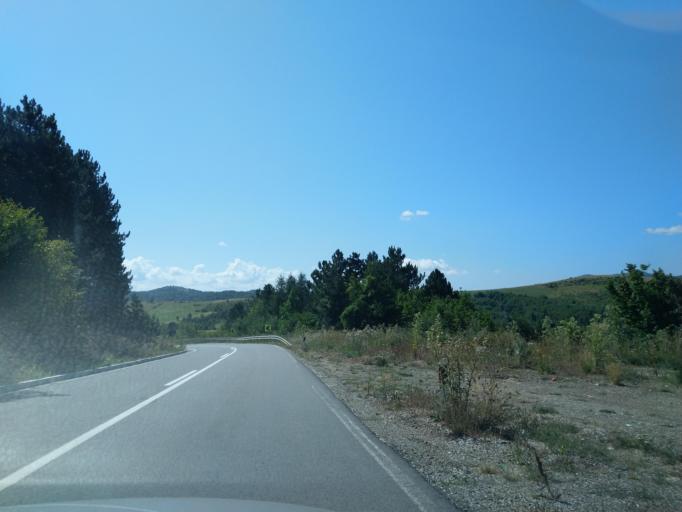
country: RS
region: Central Serbia
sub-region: Zlatiborski Okrug
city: Sjenica
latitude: 43.3077
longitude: 19.9136
